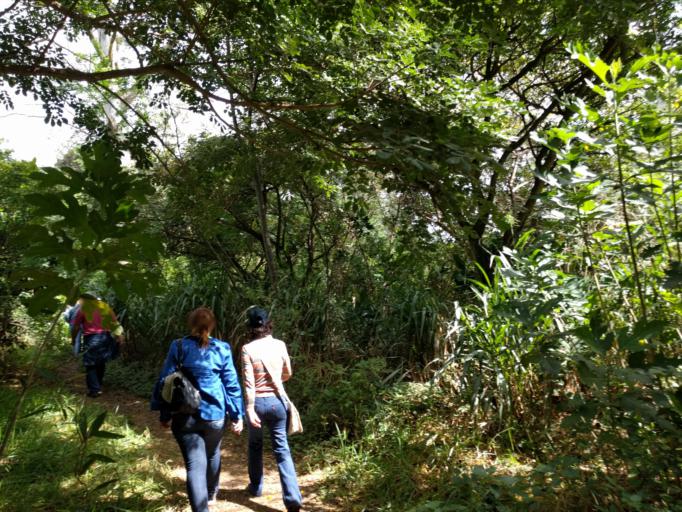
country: BO
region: Santa Cruz
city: Santa Cruz de la Sierra
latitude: -17.7954
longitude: -63.2247
